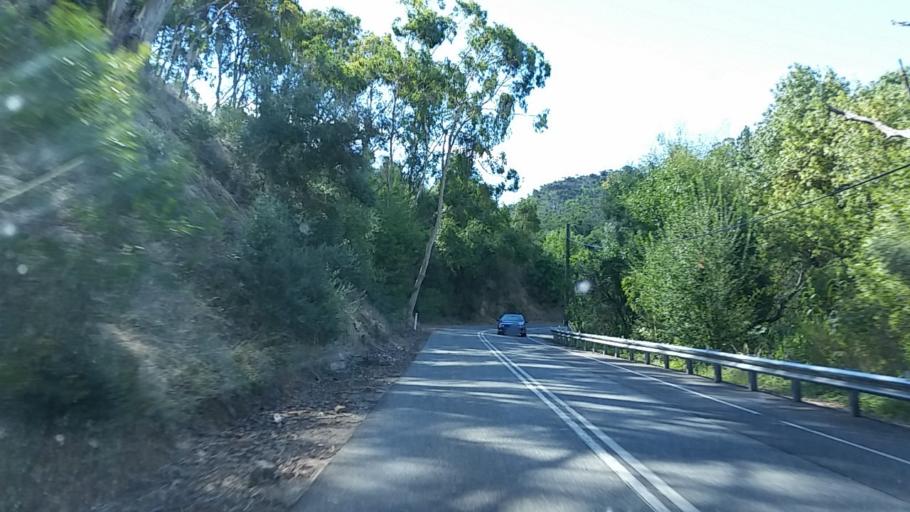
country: AU
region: South Australia
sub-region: Campbelltown
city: Athelstone
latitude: -34.8675
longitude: 138.7516
